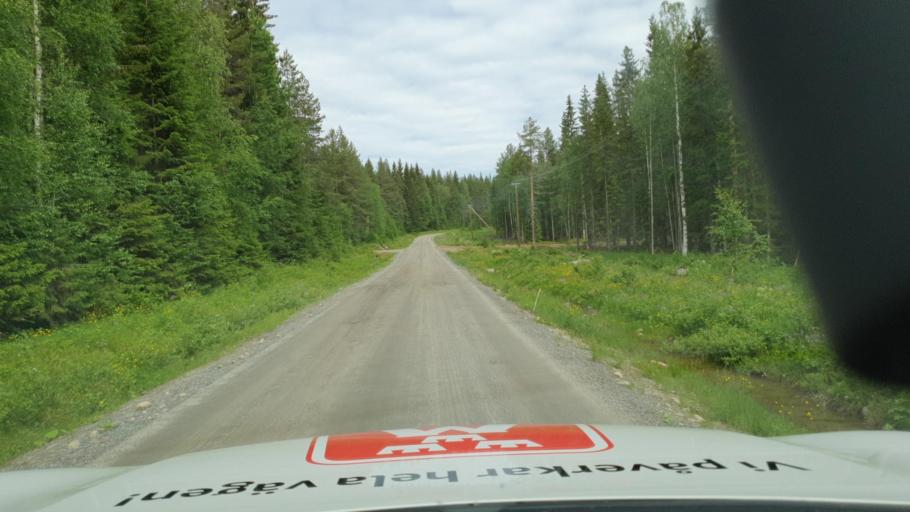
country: SE
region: Vaesterbotten
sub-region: Skelleftea Kommun
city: Langsele
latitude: 64.5511
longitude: 20.2841
